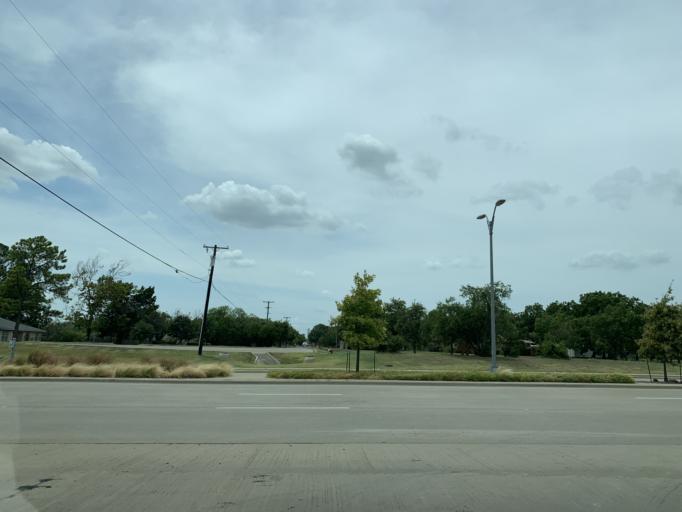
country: US
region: Texas
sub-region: Dallas County
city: Grand Prairie
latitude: 32.6702
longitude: -97.0233
